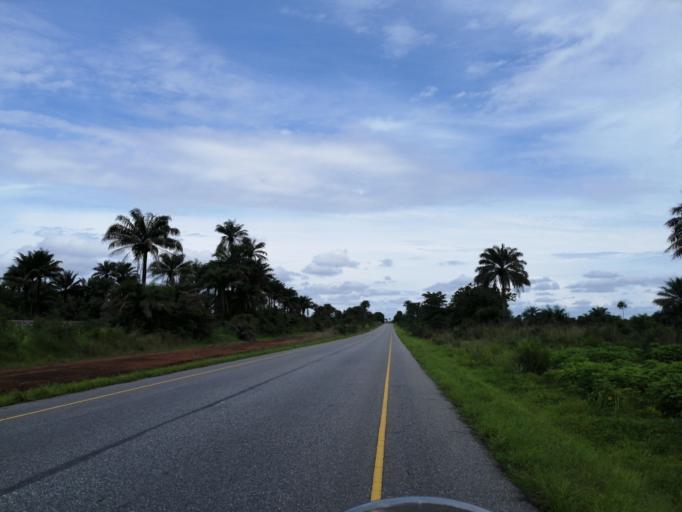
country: SL
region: Northern Province
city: Port Loko
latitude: 8.7400
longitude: -12.9419
